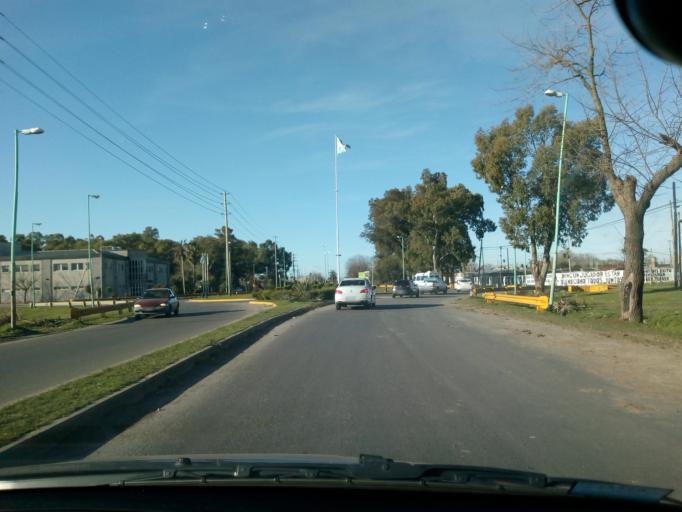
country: AR
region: Buenos Aires
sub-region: Partido de Ensenada
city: Ensenada
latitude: -34.8727
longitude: -57.9141
